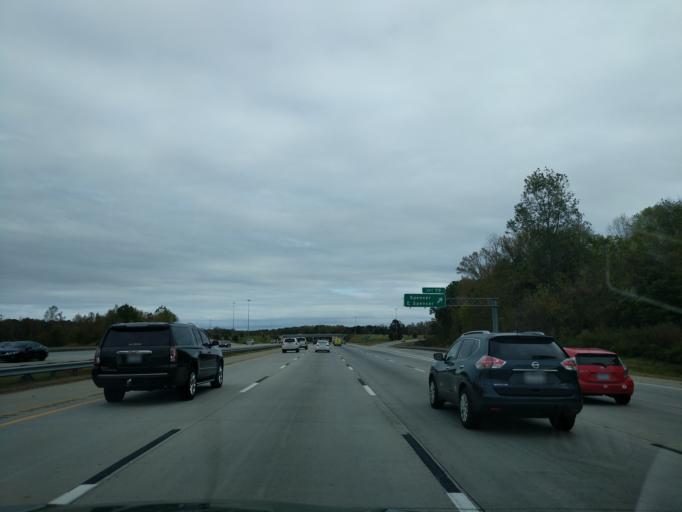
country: US
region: North Carolina
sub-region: Rowan County
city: East Spencer
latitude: 35.6755
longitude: -80.4204
